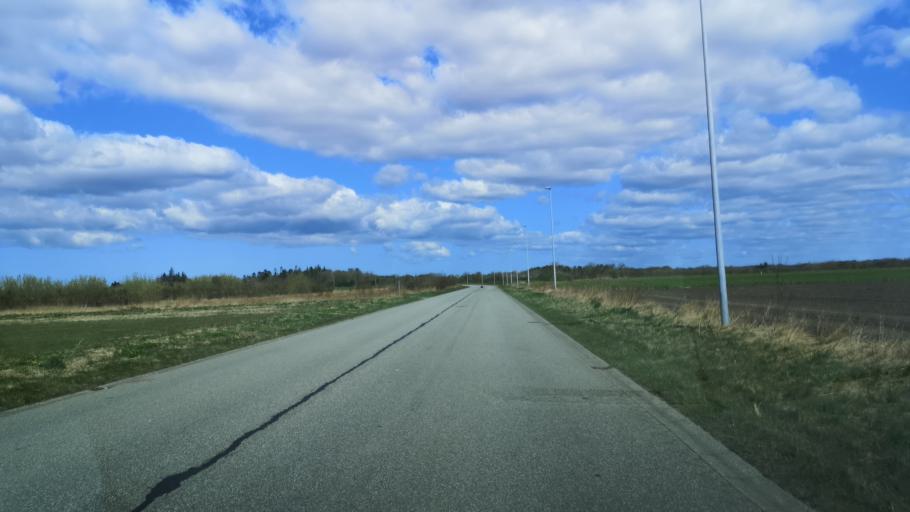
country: DK
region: Central Jutland
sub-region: Ringkobing-Skjern Kommune
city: Skjern
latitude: 55.9580
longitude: 8.5137
